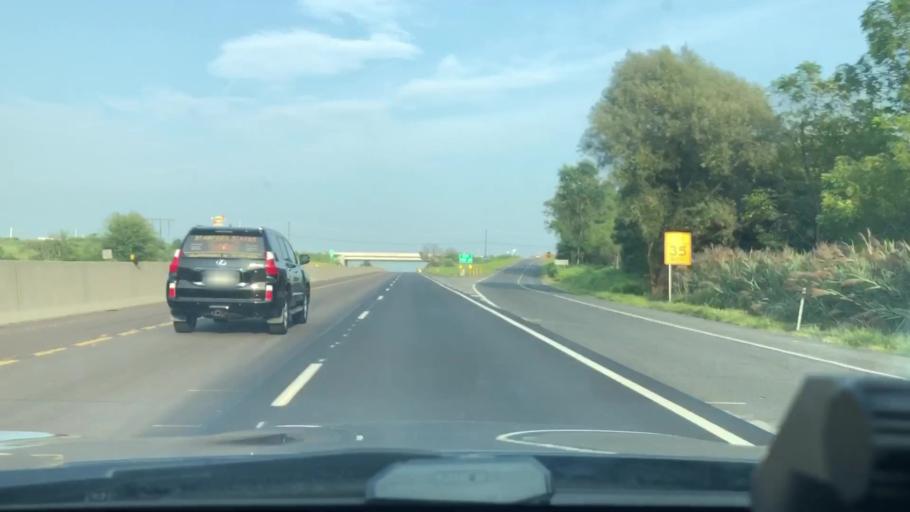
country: US
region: Pennsylvania
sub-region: Berks County
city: Topton
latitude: 40.5813
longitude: -75.7119
